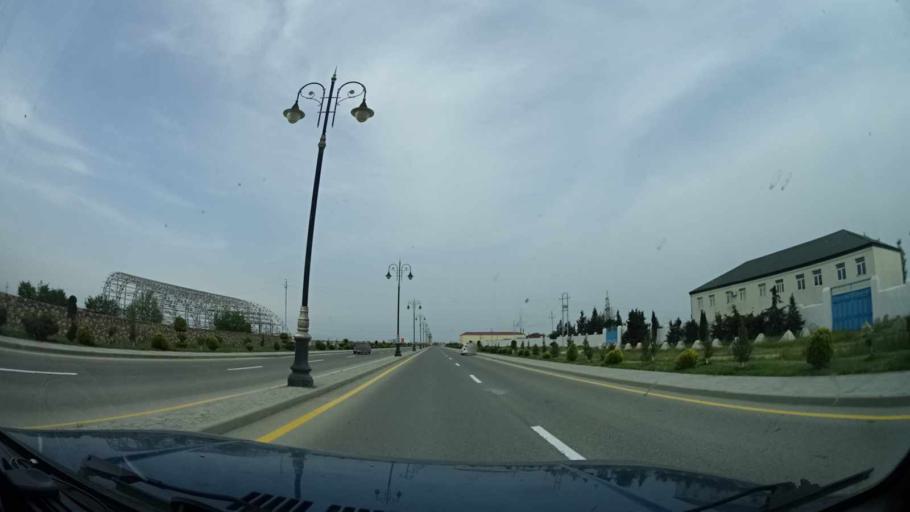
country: AZ
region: Siazan Rayon
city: Kyzyl-Burun
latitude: 41.0675
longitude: 49.1270
